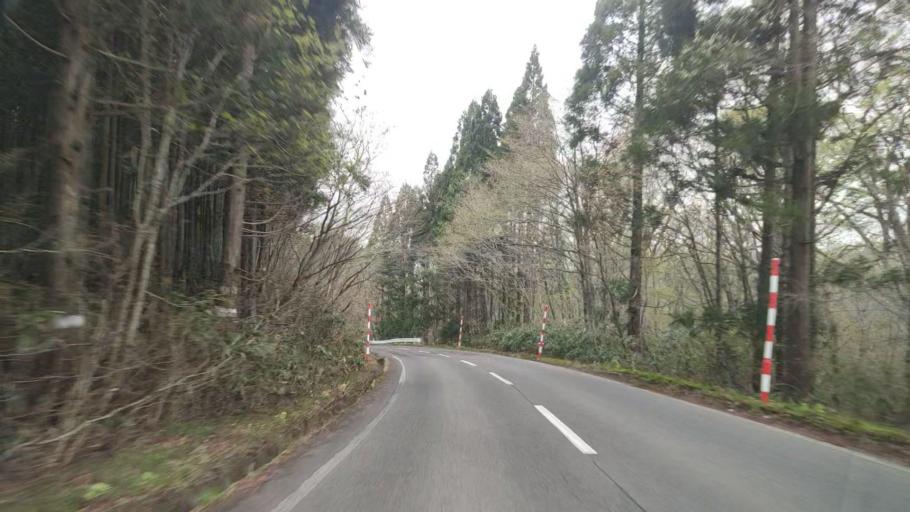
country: JP
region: Akita
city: Hanawa
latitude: 40.3965
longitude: 140.7984
